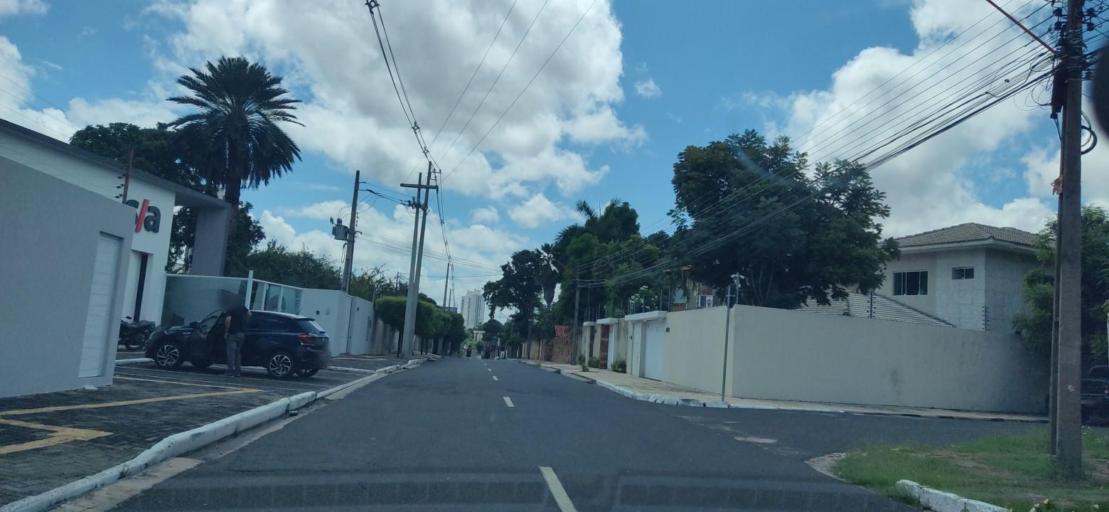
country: BR
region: Piaui
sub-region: Teresina
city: Teresina
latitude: -5.0653
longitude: -42.7803
